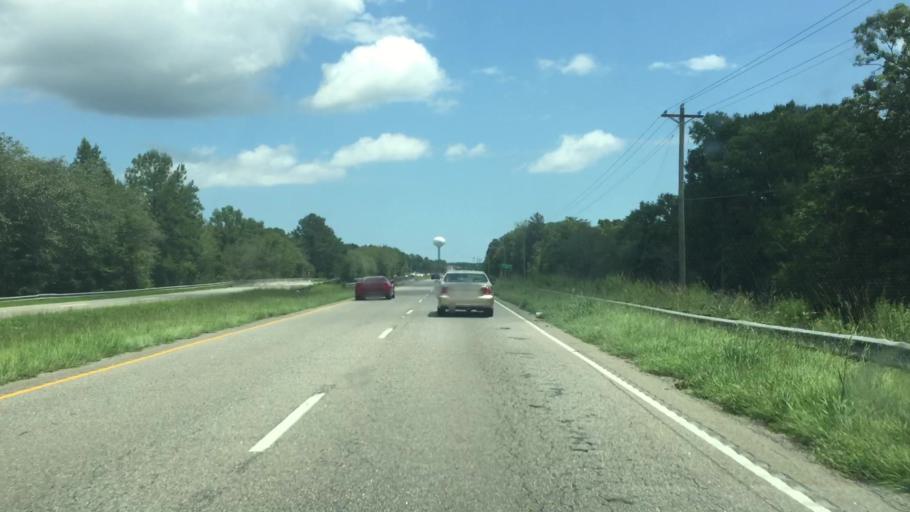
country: US
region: South Carolina
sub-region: Horry County
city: North Myrtle Beach
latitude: 33.9098
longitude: -78.7115
